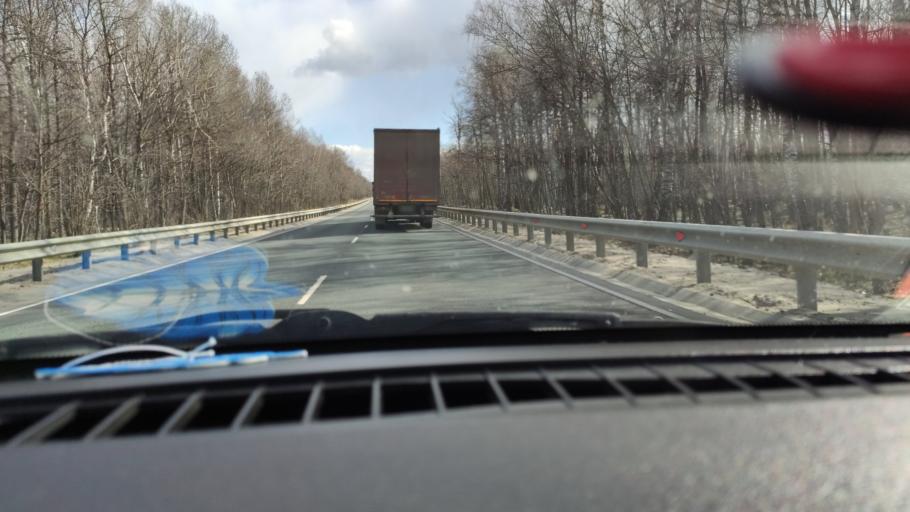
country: RU
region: Saratov
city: Khvalynsk
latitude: 52.4670
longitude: 48.0169
